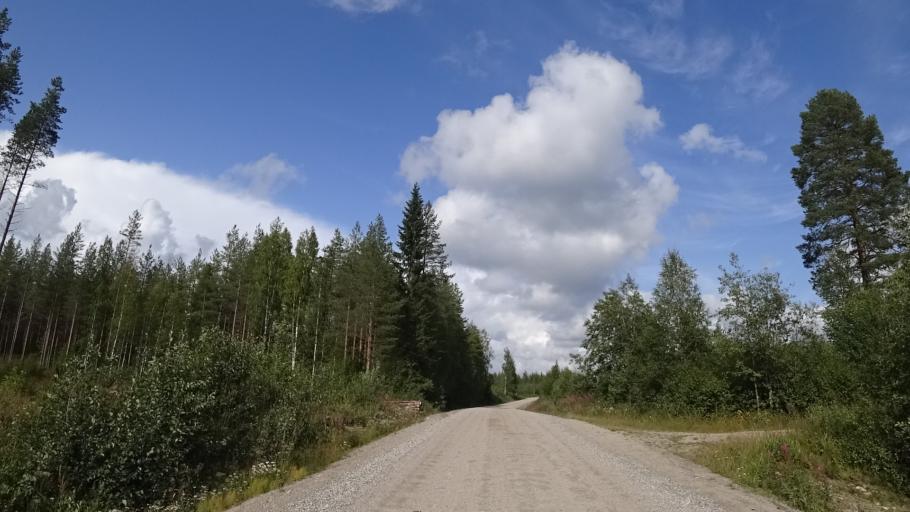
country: FI
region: North Karelia
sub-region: Pielisen Karjala
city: Lieksa
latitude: 63.5779
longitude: 30.1255
